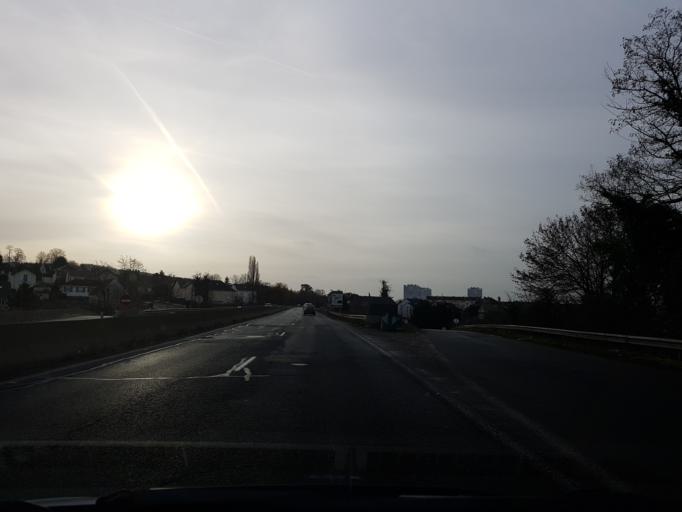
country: FR
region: Ile-de-France
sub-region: Departement de l'Essonne
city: Montgeron
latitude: 48.7088
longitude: 2.4419
